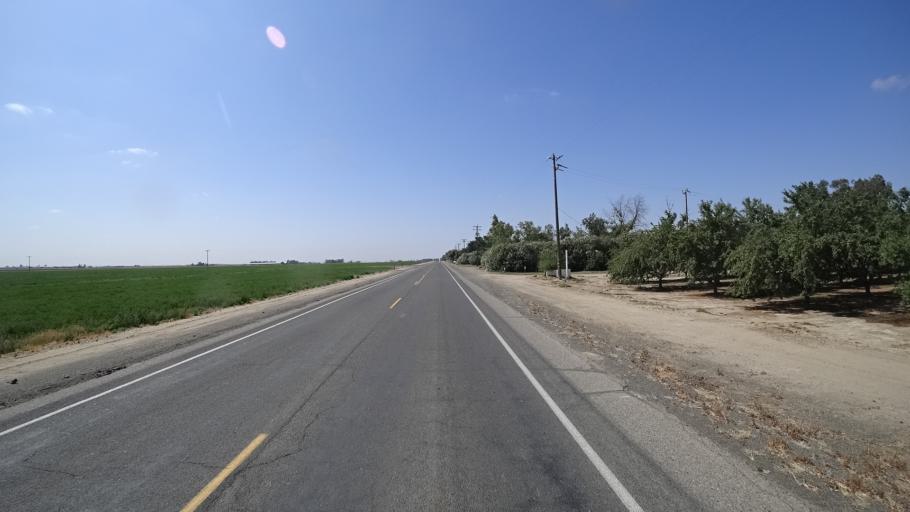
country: US
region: California
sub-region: Kings County
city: Home Garden
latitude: 36.2419
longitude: -119.6369
